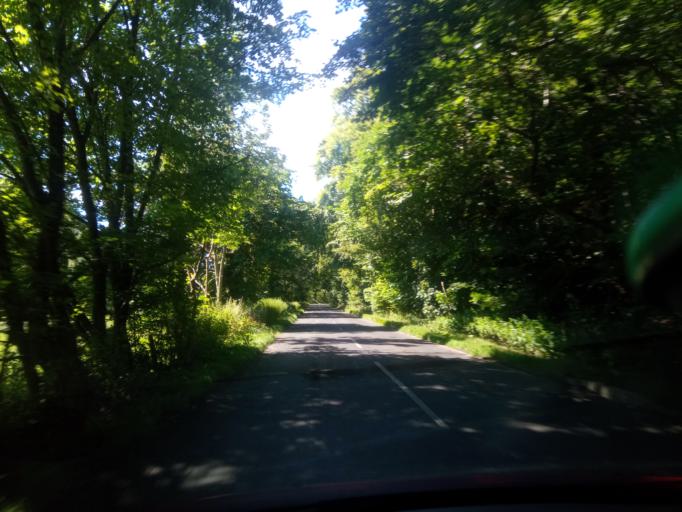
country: GB
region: England
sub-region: Northumberland
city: Bardon Mill
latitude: 54.9196
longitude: -2.3256
